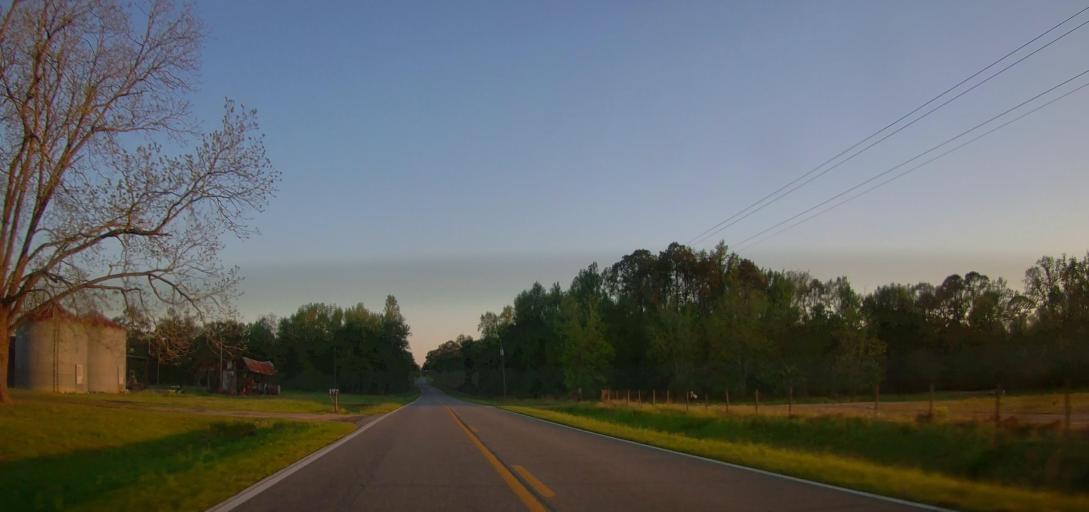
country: US
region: Georgia
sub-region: Ben Hill County
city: Fitzgerald
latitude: 31.7259
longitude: -83.3099
